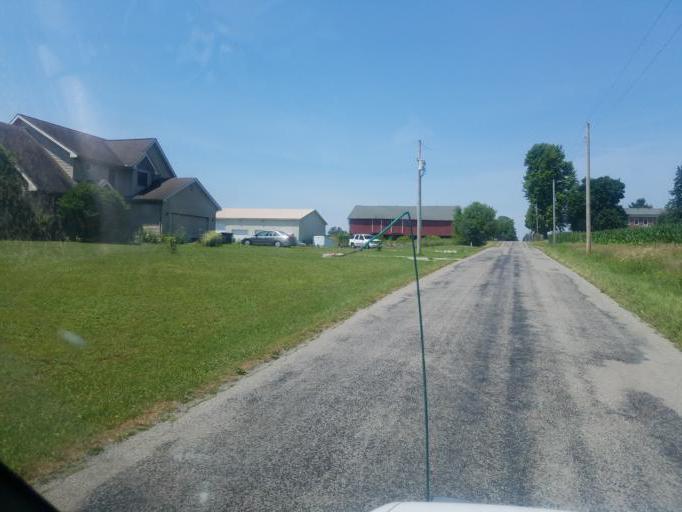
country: US
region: Ohio
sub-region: Logan County
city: West Liberty
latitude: 40.2894
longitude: -83.7836
